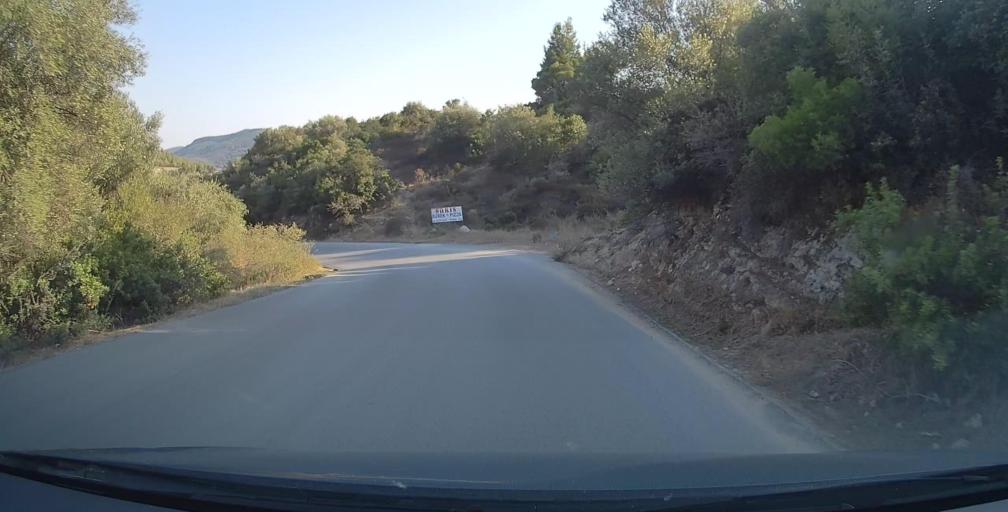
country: GR
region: Central Macedonia
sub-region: Nomos Chalkidikis
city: Sykia
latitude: 39.9986
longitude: 23.8886
